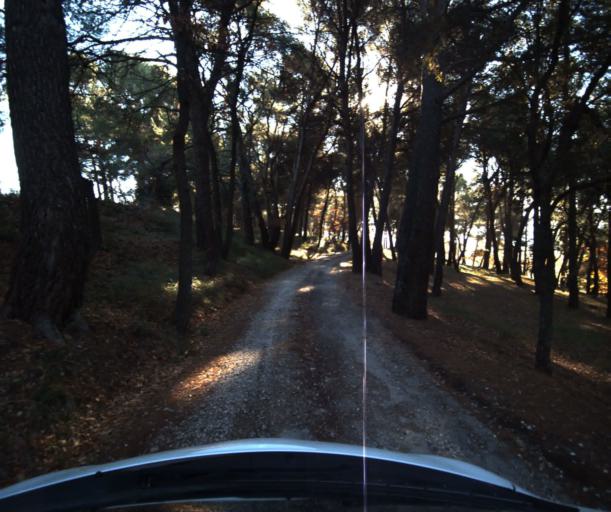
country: FR
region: Provence-Alpes-Cote d'Azur
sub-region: Departement du Vaucluse
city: Pertuis
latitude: 43.7180
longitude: 5.4923
